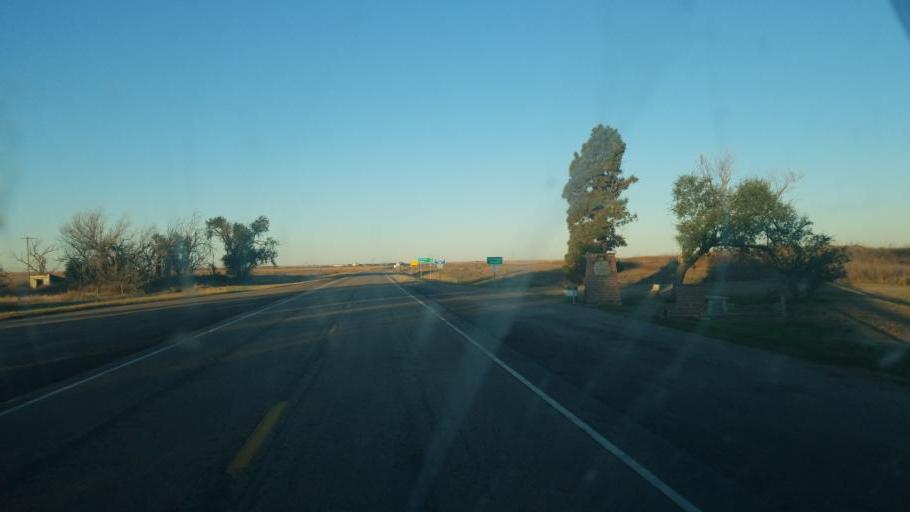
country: US
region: Kansas
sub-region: Wallace County
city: Sharon Springs
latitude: 38.8575
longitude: -102.0456
